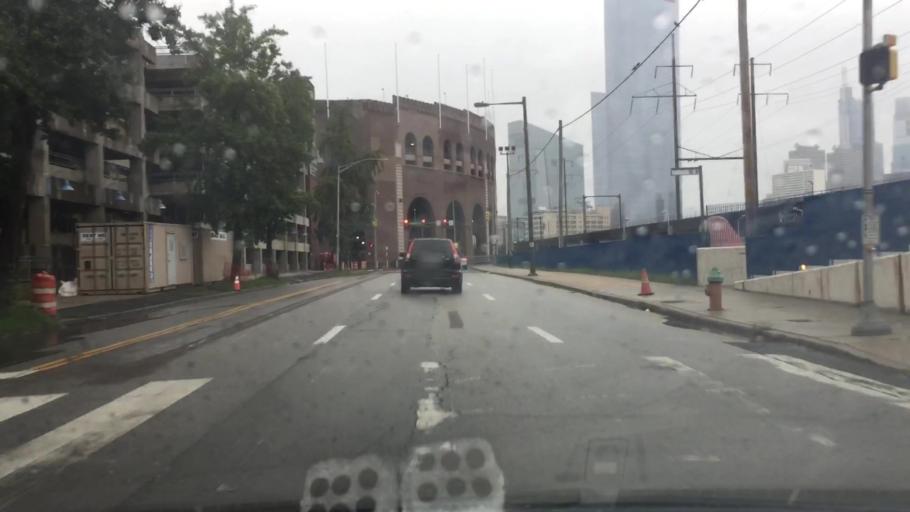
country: US
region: Pennsylvania
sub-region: Philadelphia County
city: Philadelphia
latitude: 39.9481
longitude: -75.1906
